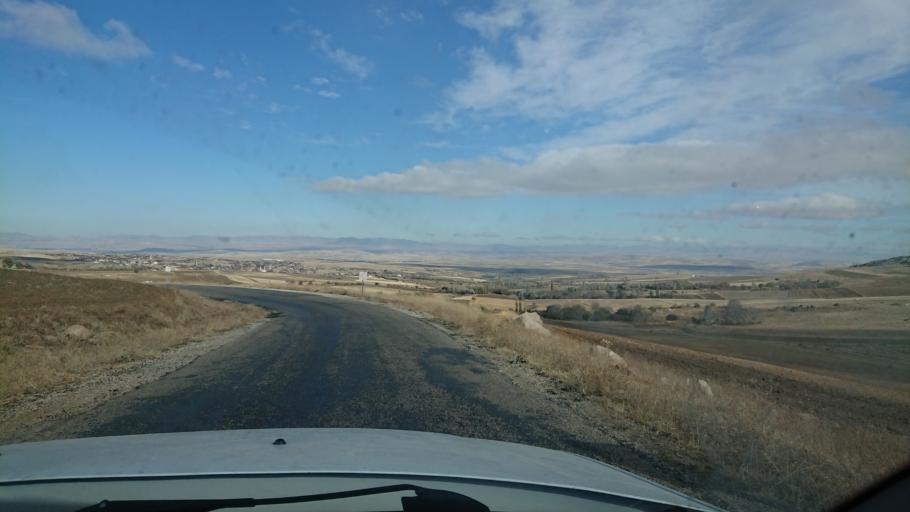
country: TR
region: Aksaray
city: Agacoren
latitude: 38.8428
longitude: 33.9528
